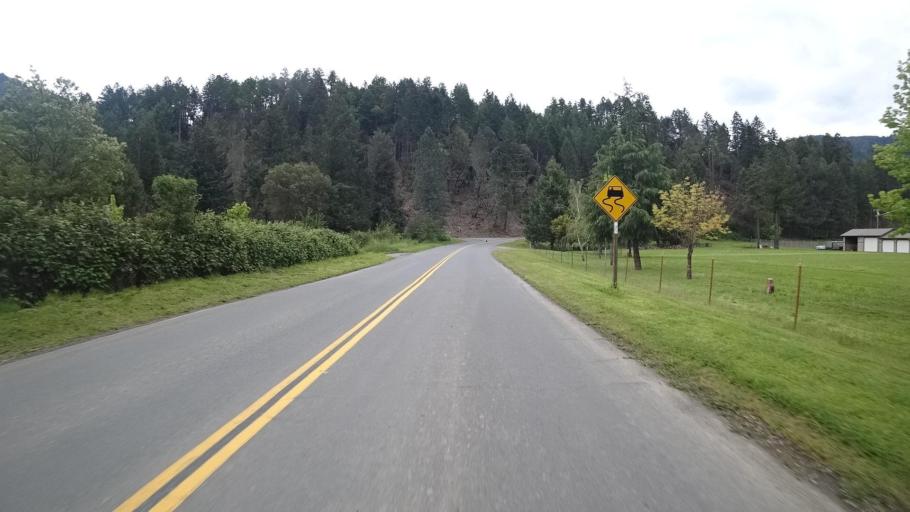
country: US
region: California
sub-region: Humboldt County
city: Willow Creek
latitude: 40.9428
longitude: -123.6227
